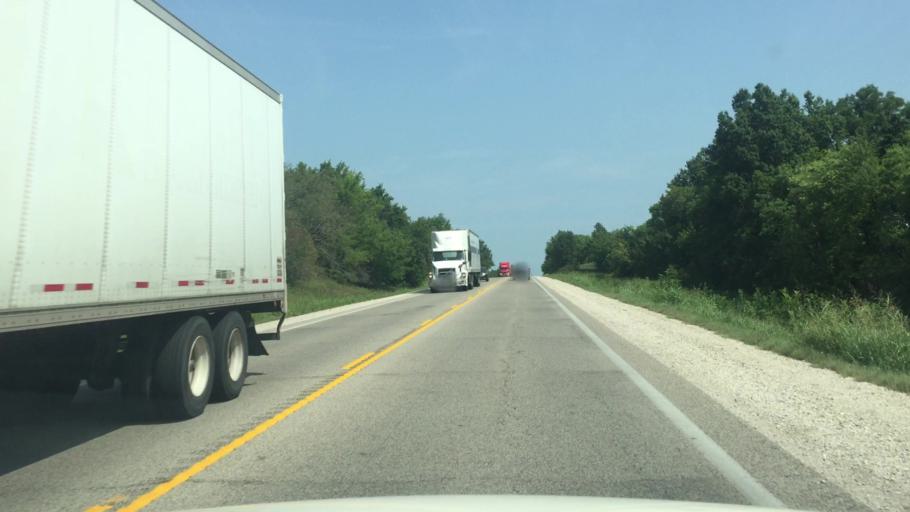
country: US
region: Kansas
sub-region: Montgomery County
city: Coffeyville
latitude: 37.1467
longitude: -95.5768
